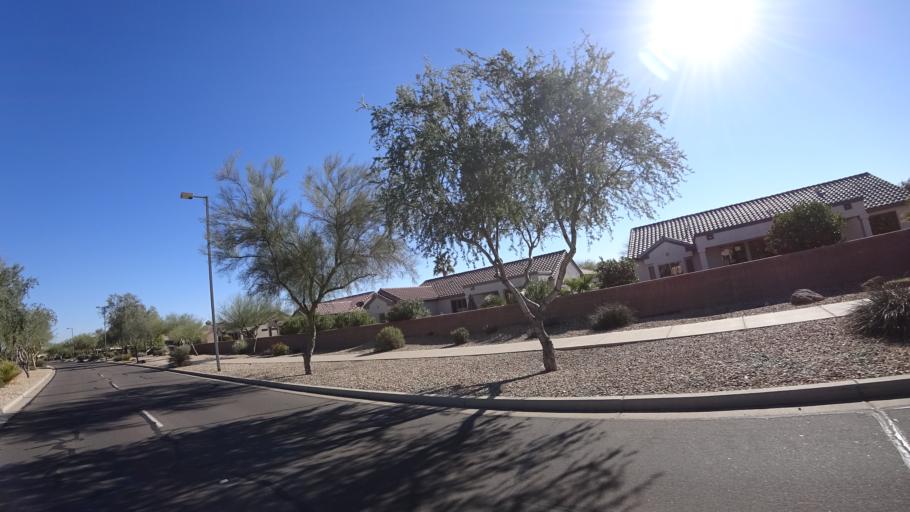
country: US
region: Arizona
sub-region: Maricopa County
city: Sun City West
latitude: 33.6696
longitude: -112.4074
